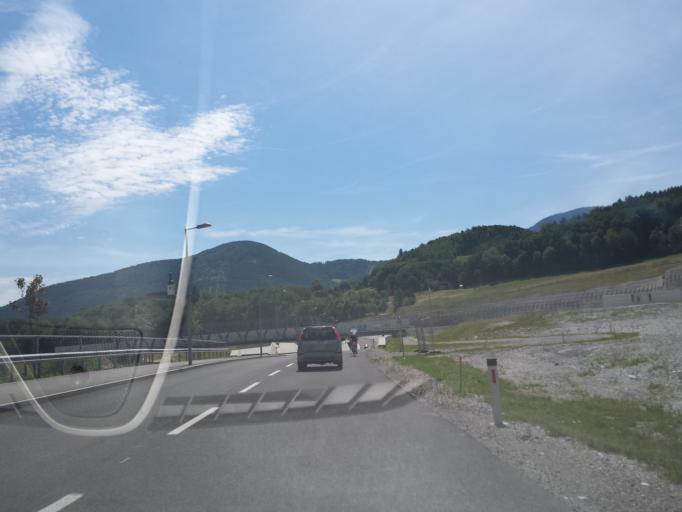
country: AT
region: Lower Austria
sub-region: Politischer Bezirk Neunkirchen
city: Gloggnitz
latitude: 47.6791
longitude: 15.9244
